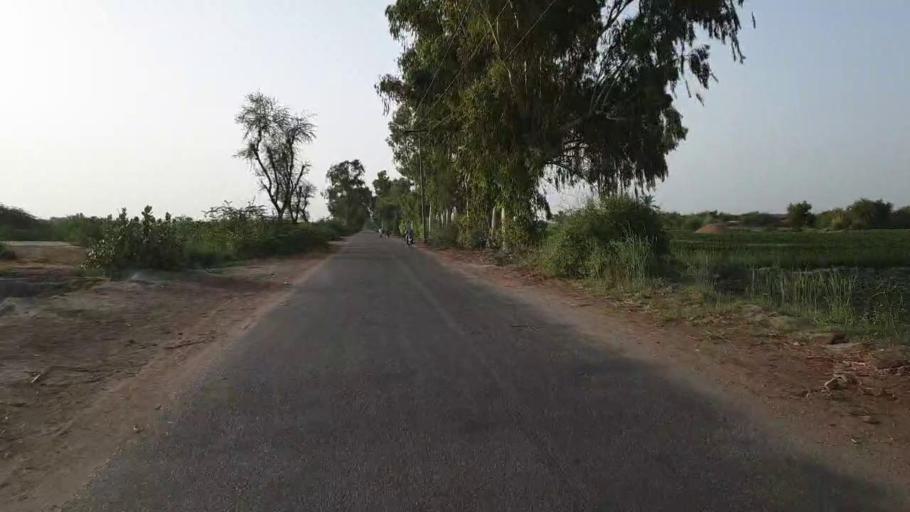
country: PK
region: Sindh
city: Bozdar
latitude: 27.1064
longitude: 68.9613
